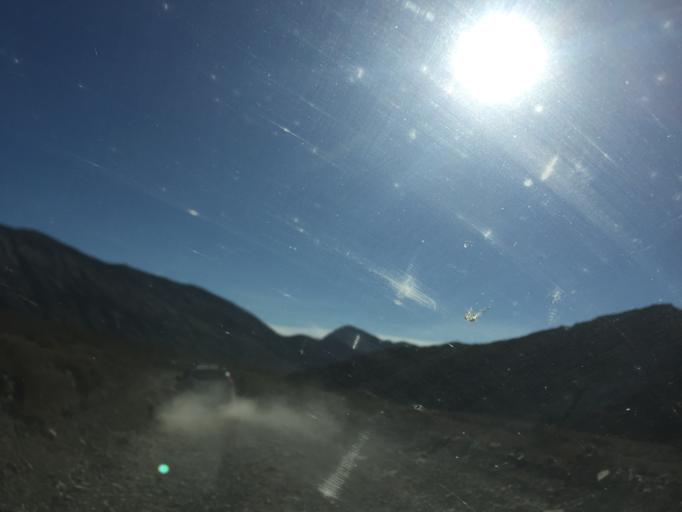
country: US
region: California
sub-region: Inyo County
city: Lone Pine
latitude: 36.7890
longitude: -117.5200
